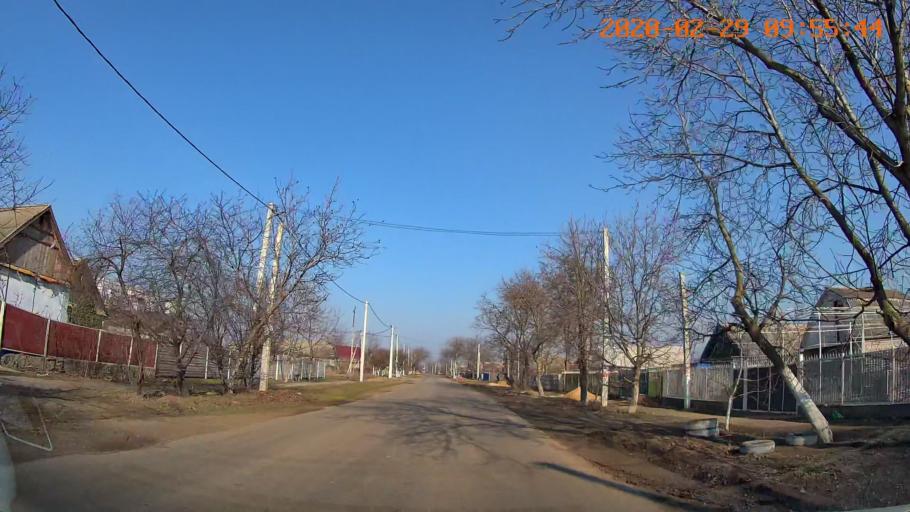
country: MD
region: Telenesti
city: Slobozia
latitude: 46.7364
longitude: 29.7087
